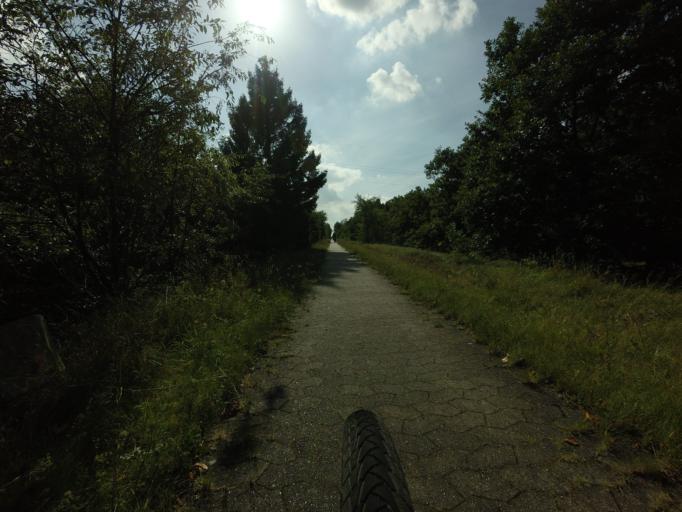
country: DK
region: Central Jutland
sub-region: Viborg Kommune
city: Karup
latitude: 56.2676
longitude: 9.1145
